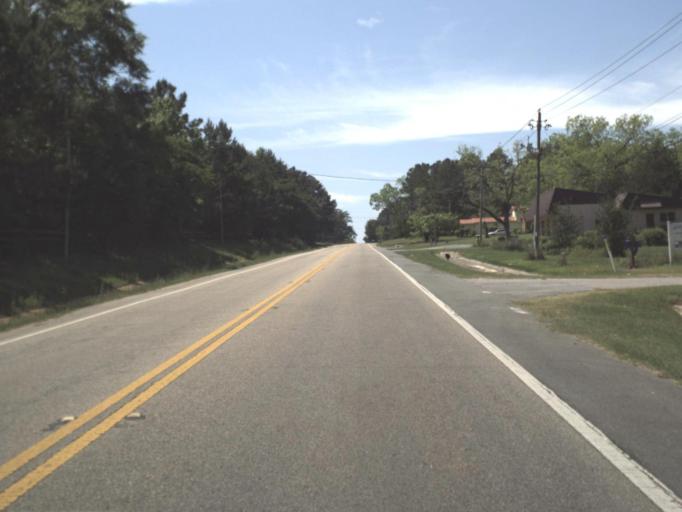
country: US
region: Florida
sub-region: Jackson County
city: Marianna
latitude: 30.7614
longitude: -85.2295
